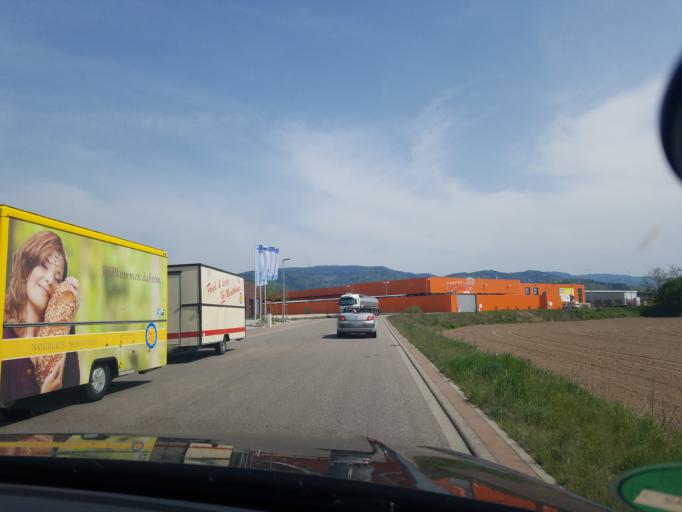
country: DE
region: Baden-Wuerttemberg
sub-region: Freiburg Region
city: Achern
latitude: 48.6349
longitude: 8.0549
